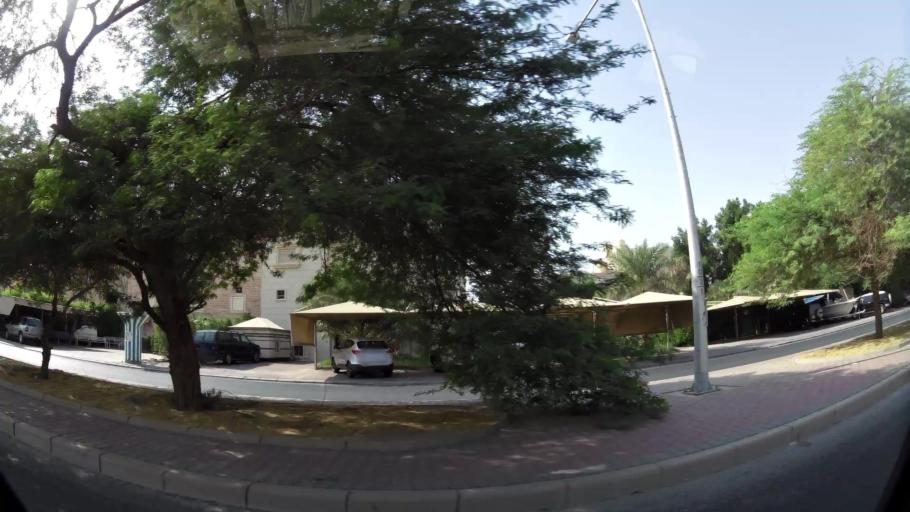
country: KW
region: Muhafazat al Jahra'
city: Al Jahra'
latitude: 29.3185
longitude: 47.6784
